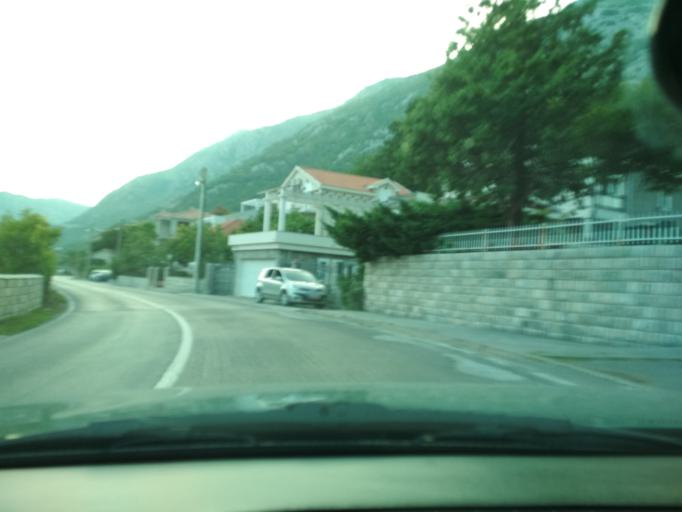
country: ME
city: Lipci
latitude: 42.5054
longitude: 18.6724
